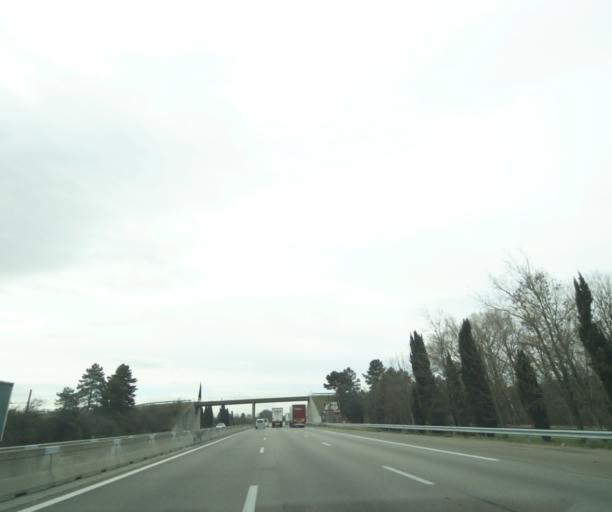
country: FR
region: Rhone-Alpes
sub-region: Departement de la Drome
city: Livron-sur-Drome
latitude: 44.8091
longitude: 4.8538
